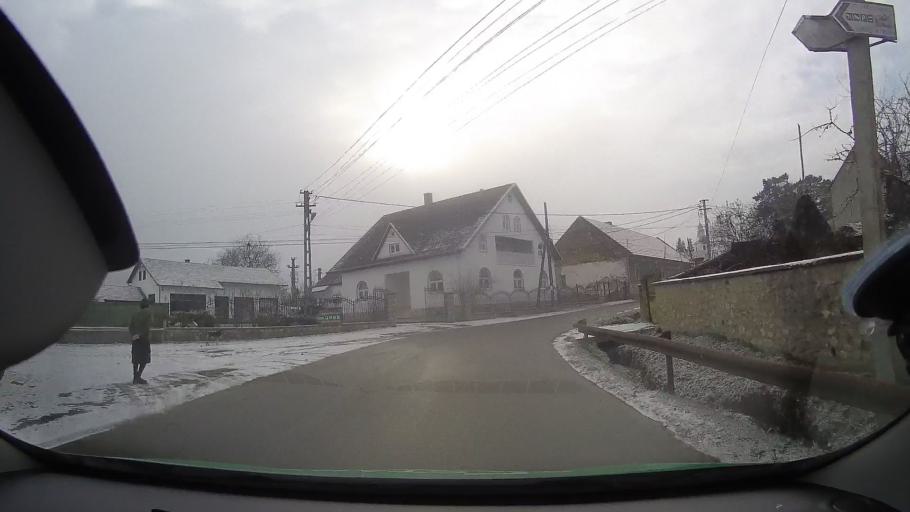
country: RO
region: Alba
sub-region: Comuna Rimetea
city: Rimetea
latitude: 46.4238
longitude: 23.5622
